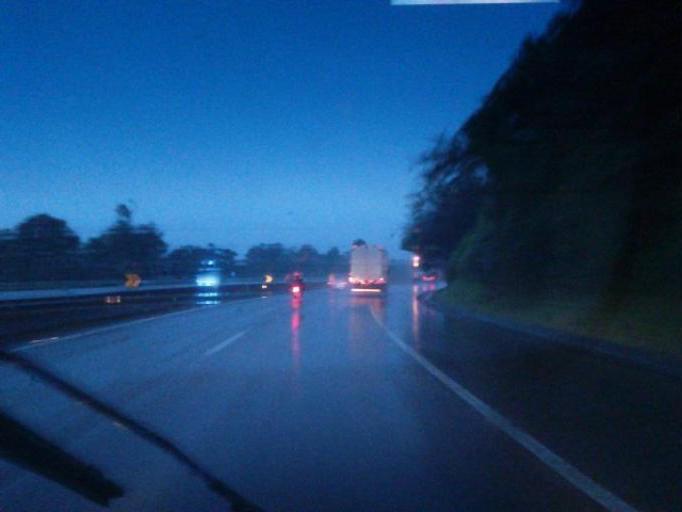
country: BR
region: Sao Paulo
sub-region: Juquitiba
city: Juquitiba
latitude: -23.9354
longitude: -47.0336
